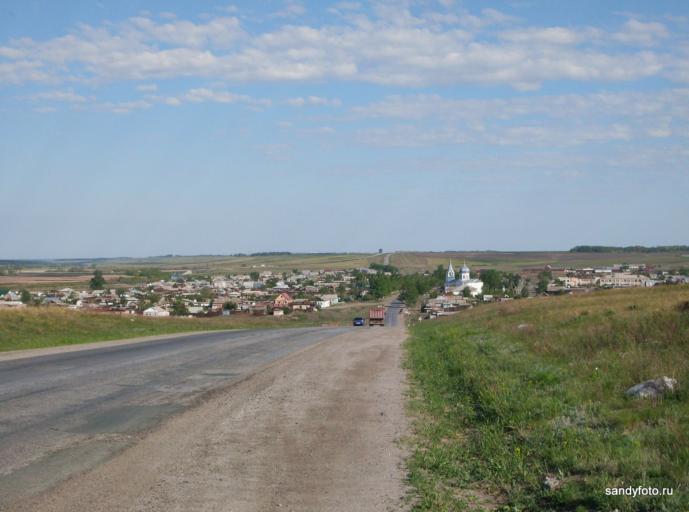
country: RU
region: Chelyabinsk
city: Troitsk
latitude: 54.1082
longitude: 61.5141
